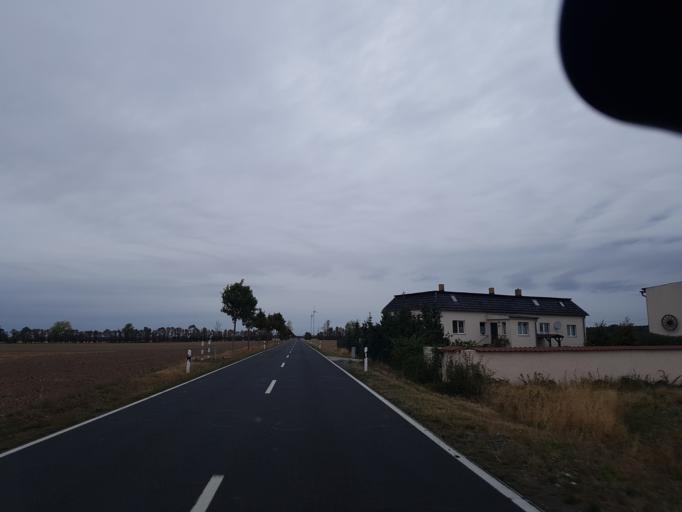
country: DE
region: Saxony-Anhalt
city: Prettin
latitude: 51.6770
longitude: 12.9093
